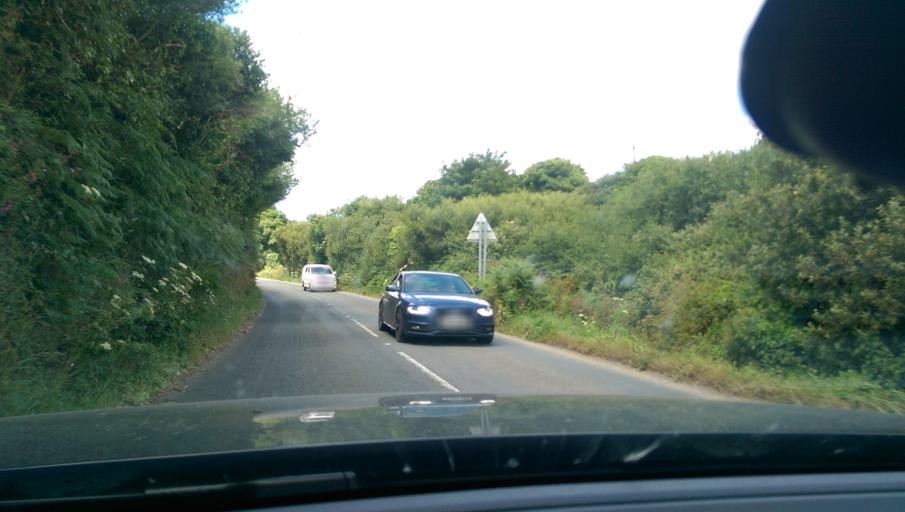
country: GB
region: England
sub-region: Cornwall
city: St. Buryan
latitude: 50.0970
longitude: -5.5963
